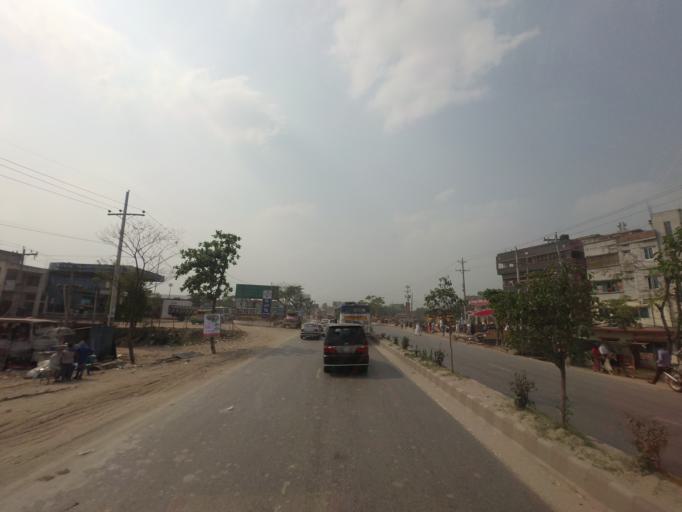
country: BD
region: Dhaka
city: Azimpur
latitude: 23.7878
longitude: 90.3274
